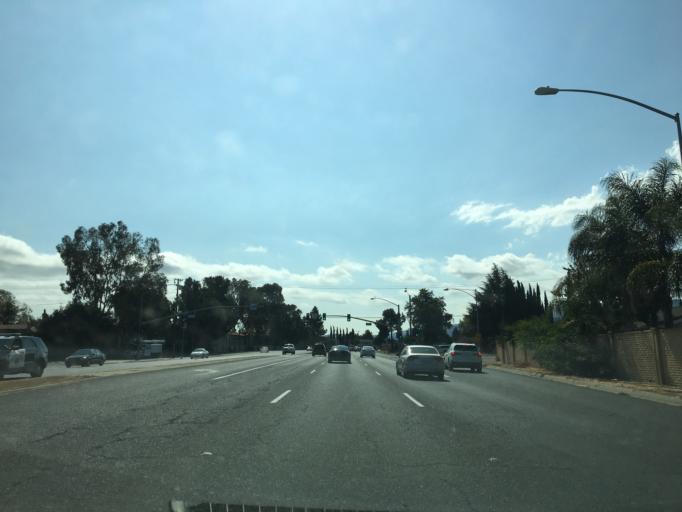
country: US
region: California
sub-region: Santa Clara County
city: Campbell
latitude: 37.2807
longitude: -121.9582
